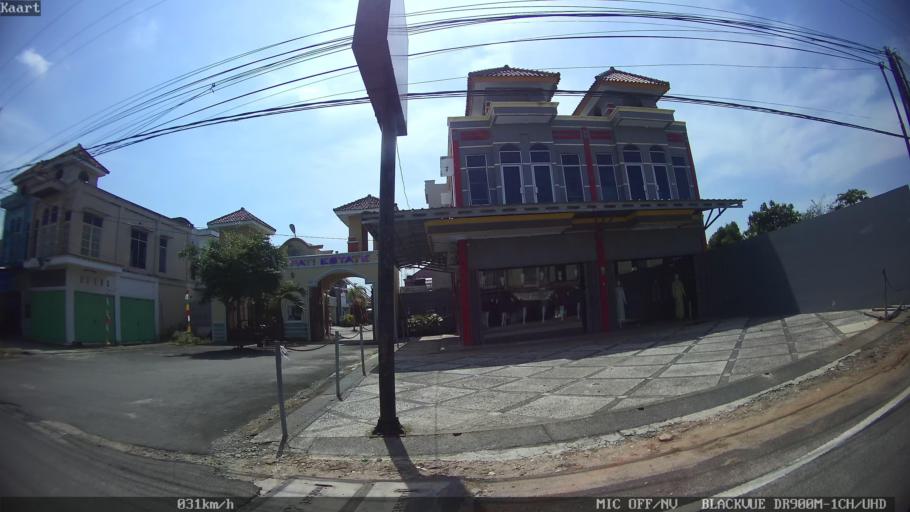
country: ID
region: Lampung
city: Kedaton
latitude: -5.3677
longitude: 105.2560
